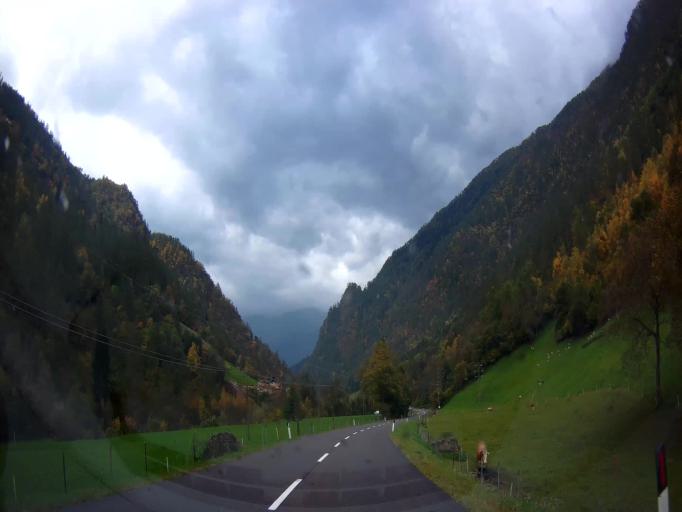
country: IT
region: Trentino-Alto Adige
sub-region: Bolzano
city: Certosa
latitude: 46.6808
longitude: 10.9362
